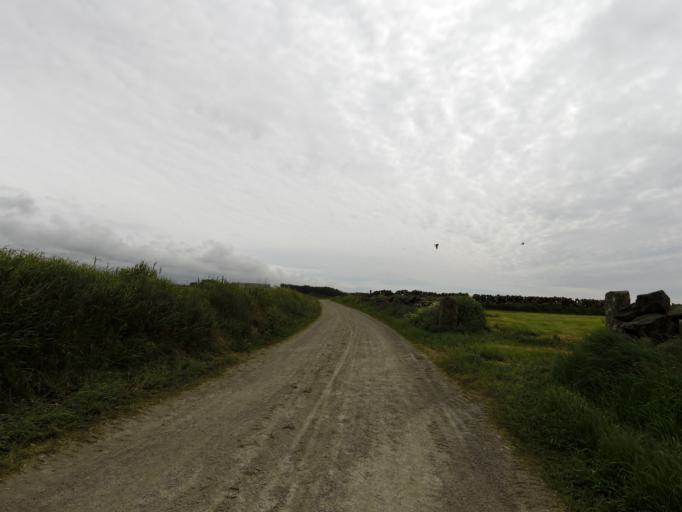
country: NO
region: Rogaland
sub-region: Ha
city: Naerbo
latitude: 58.6761
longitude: 5.5470
